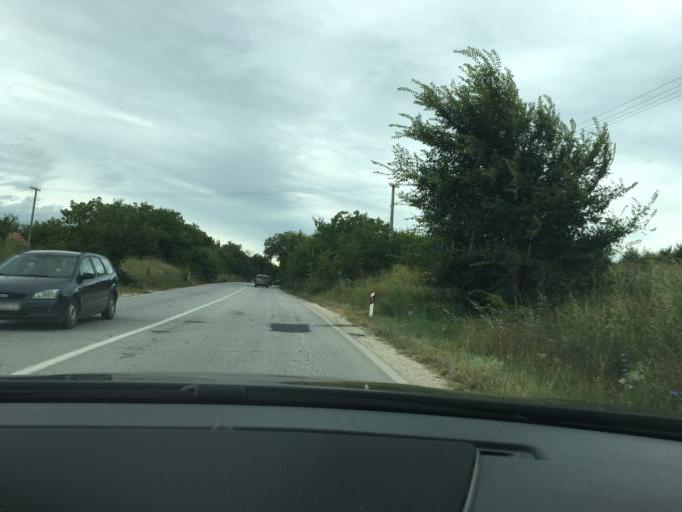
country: MK
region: Staro Nagoricane
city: Staro Nagorichane
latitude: 42.1722
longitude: 21.7751
